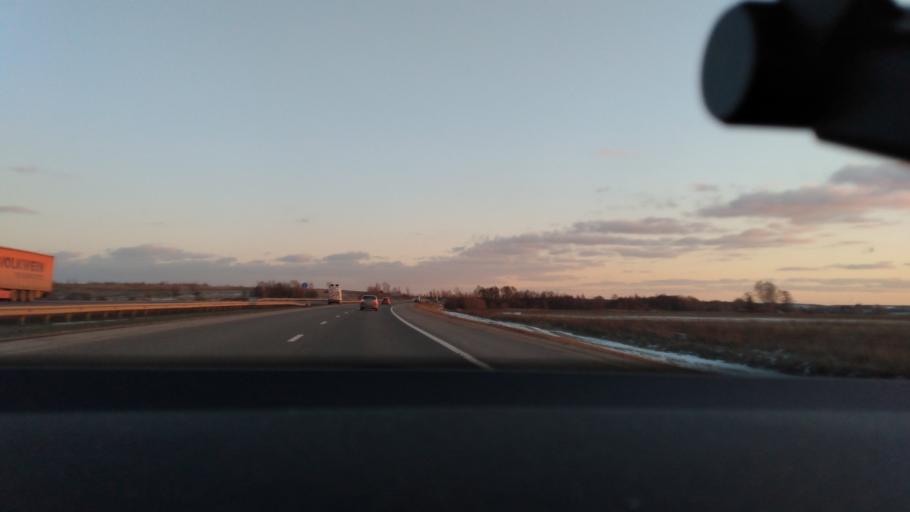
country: RU
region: Moskovskaya
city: Kolomna
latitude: 55.1023
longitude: 38.8975
